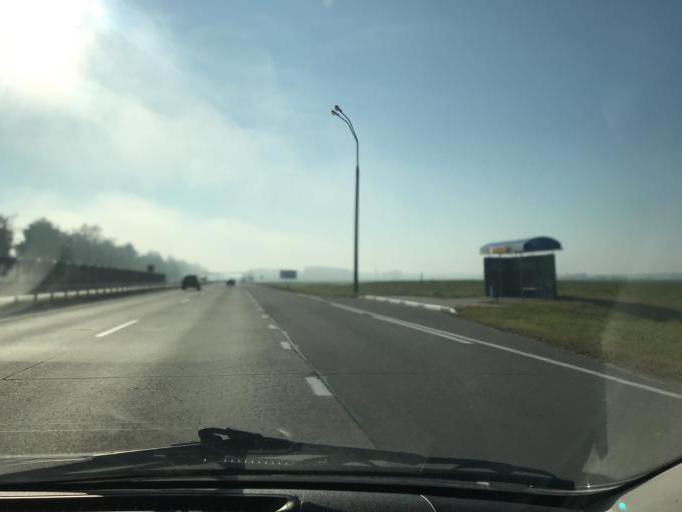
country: BY
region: Minsk
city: Samakhvalavichy
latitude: 53.5721
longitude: 27.4703
